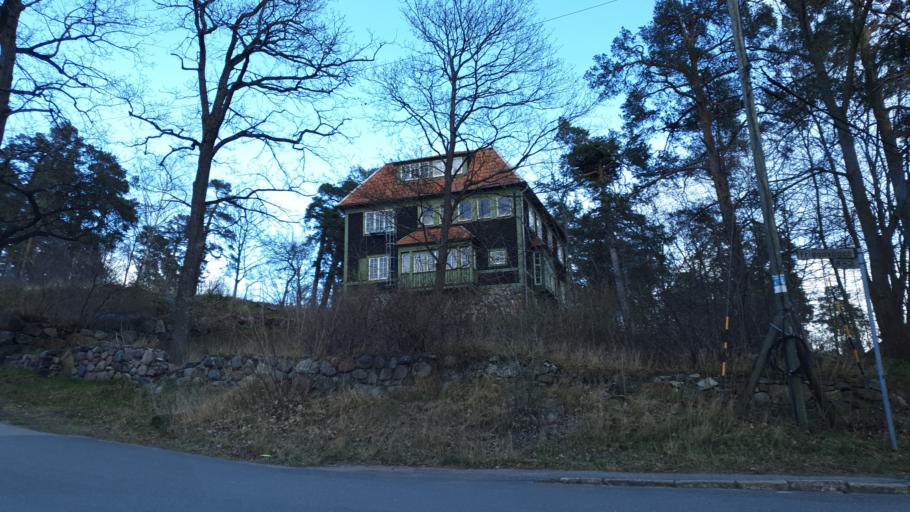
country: SE
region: Stockholm
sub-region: Lidingo
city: Lidingoe
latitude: 59.3682
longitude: 18.1265
